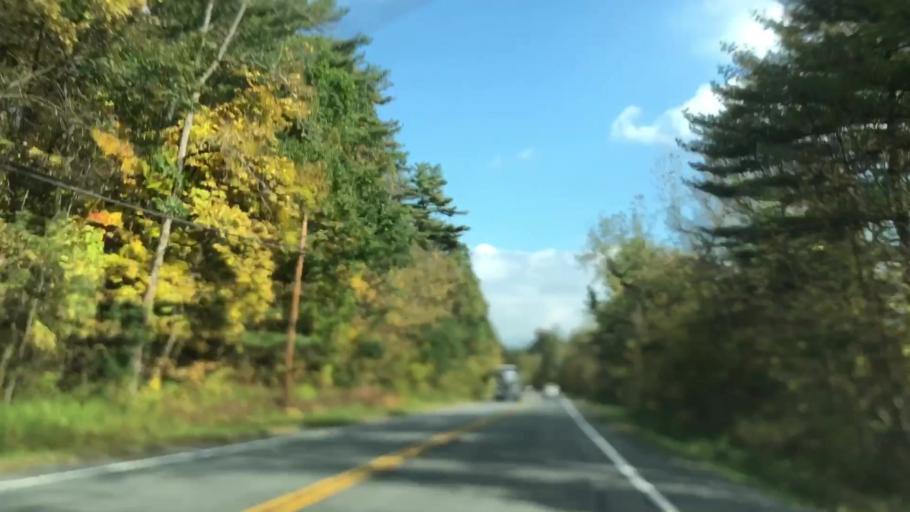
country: US
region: New York
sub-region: Warren County
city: Queensbury
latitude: 43.4256
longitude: -73.4783
